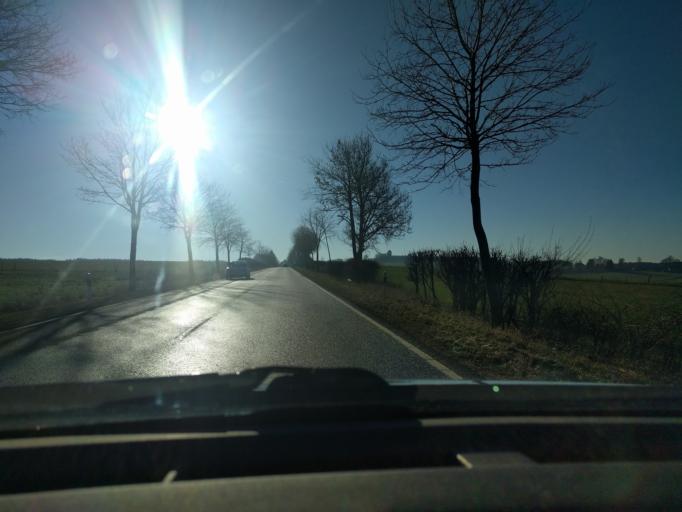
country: LU
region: Diekirch
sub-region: Canton de Clervaux
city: Troisvierges
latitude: 50.1694
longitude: 6.0255
